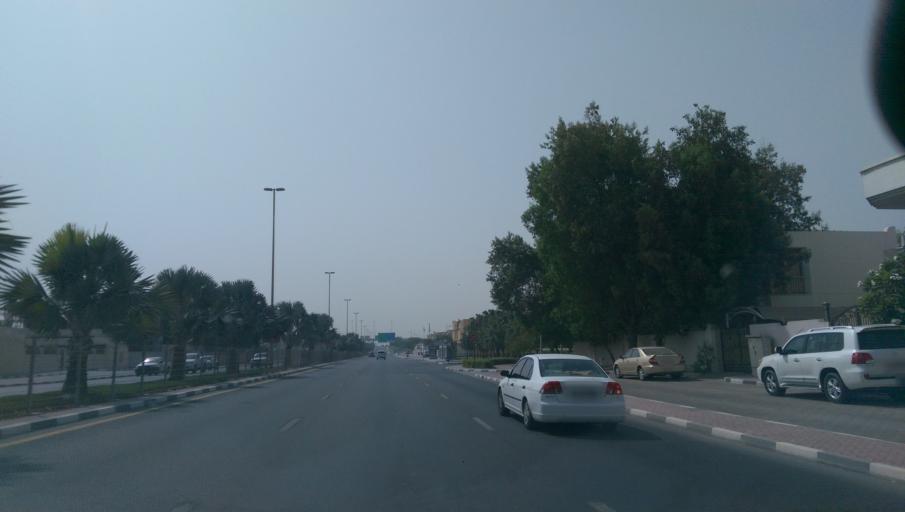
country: AE
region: Dubai
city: Dubai
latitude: 25.1532
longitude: 55.2180
